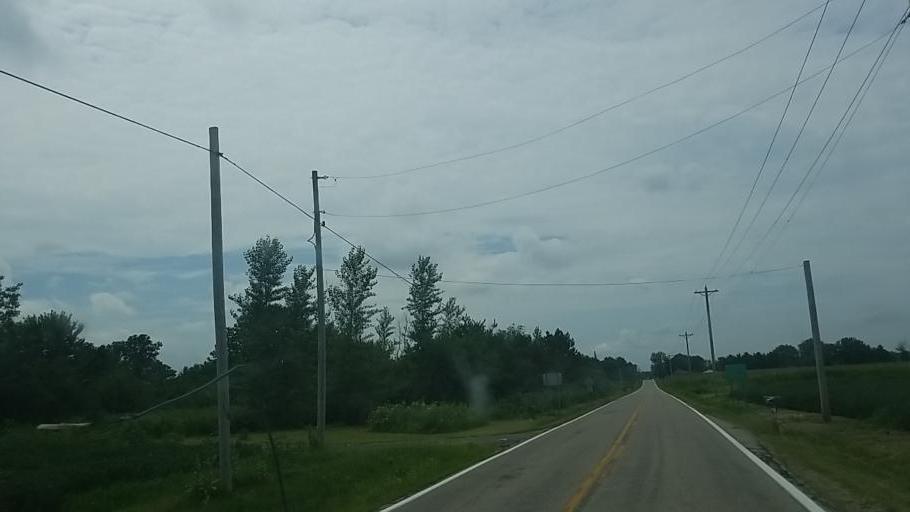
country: US
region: Ohio
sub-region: Pickaway County
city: Ashville
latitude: 39.7226
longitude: -82.9053
